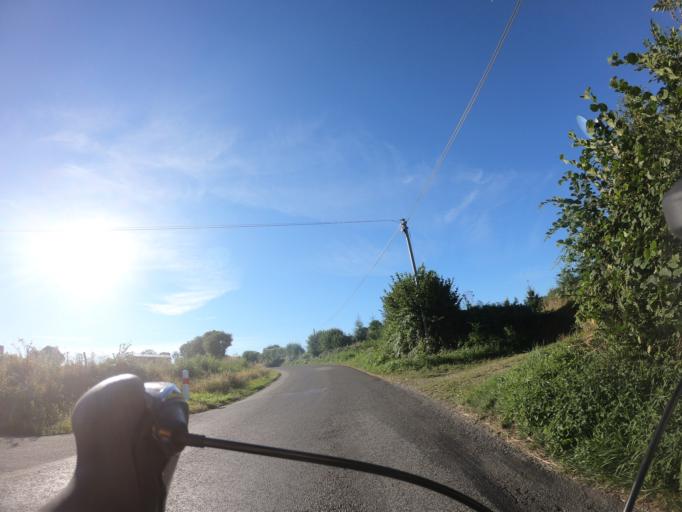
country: FR
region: Pays de la Loire
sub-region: Departement de la Mayenne
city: Pre-en-Pail
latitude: 48.5420
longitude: -0.2221
